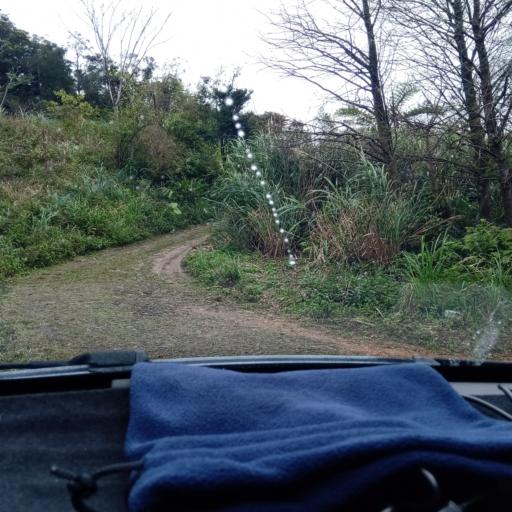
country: TW
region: Taiwan
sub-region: Yilan
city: Yilan
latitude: 24.8135
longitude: 121.6911
